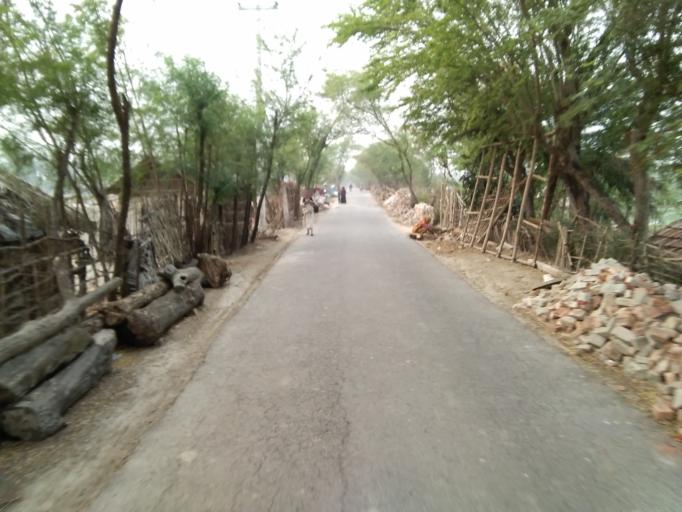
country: BD
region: Khulna
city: Satkhira
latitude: 22.5802
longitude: 89.0690
